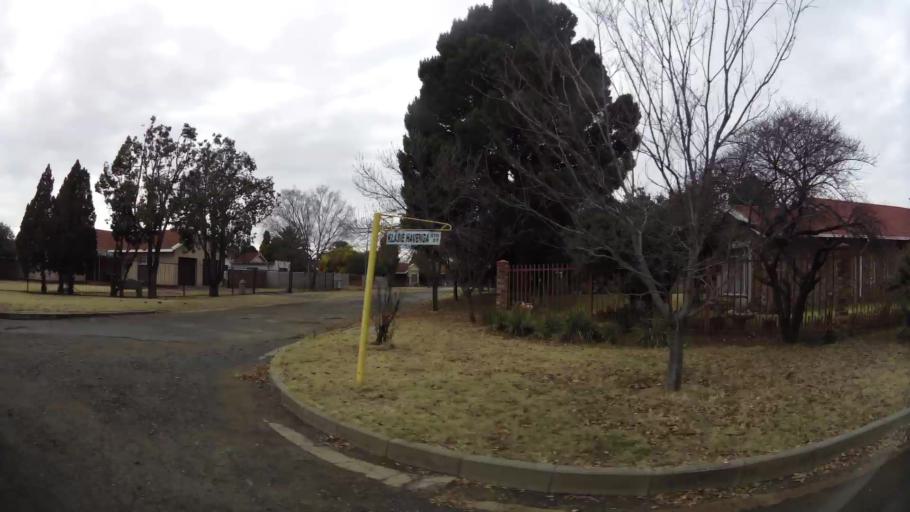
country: ZA
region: Orange Free State
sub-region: Fezile Dabi District Municipality
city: Kroonstad
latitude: -27.6345
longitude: 27.2422
